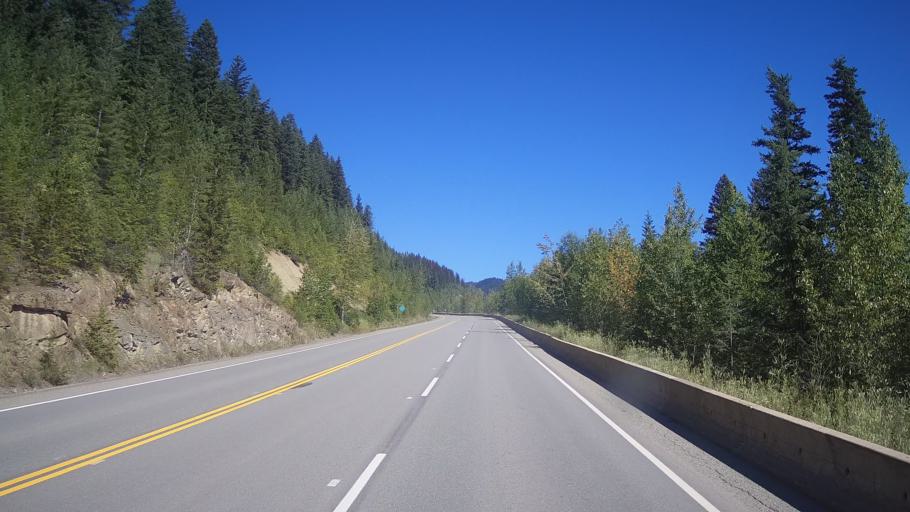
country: CA
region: British Columbia
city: Kamloops
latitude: 51.4796
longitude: -120.2597
